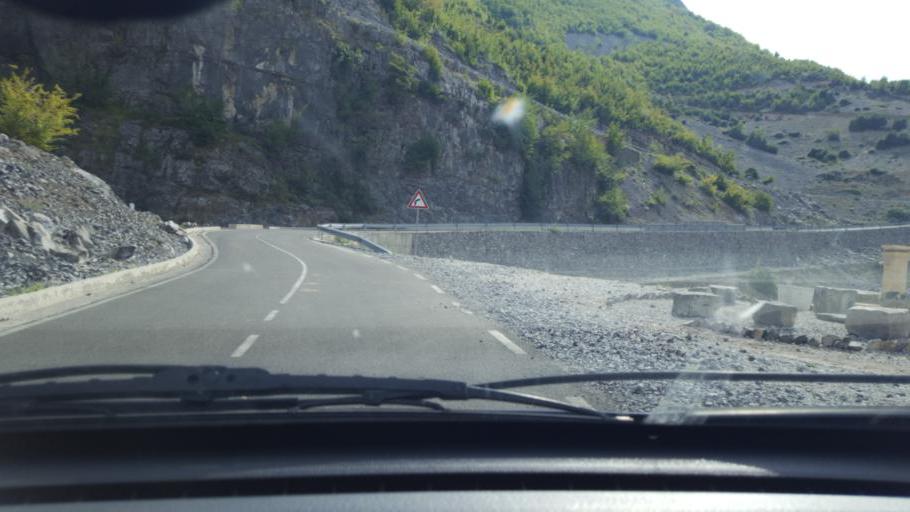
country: AL
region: Shkoder
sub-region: Rrethi i Malesia e Madhe
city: Kastrat
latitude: 42.5061
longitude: 19.6128
